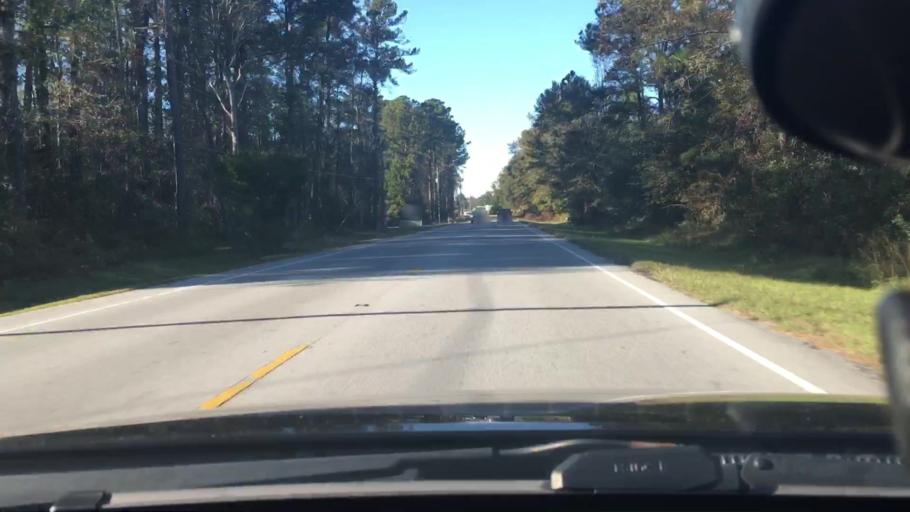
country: US
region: North Carolina
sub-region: Craven County
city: New Bern
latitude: 35.2143
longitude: -77.0630
